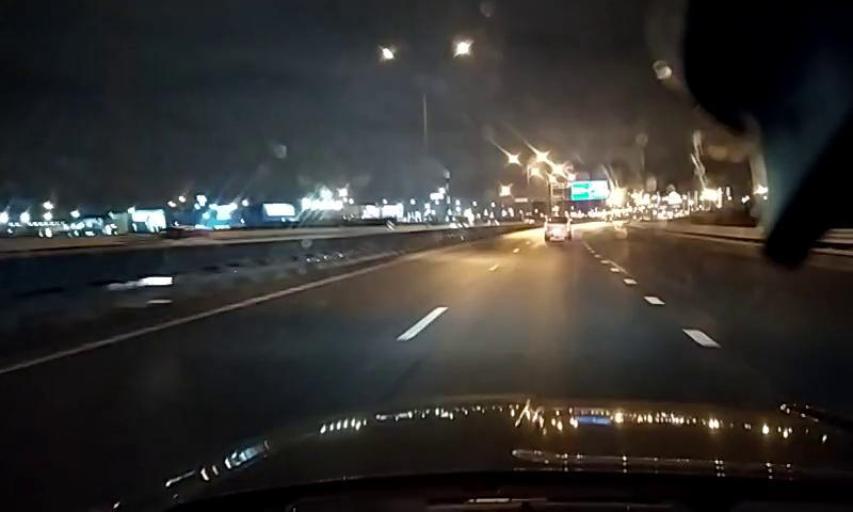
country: RU
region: Leningrad
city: Bugry
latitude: 60.0974
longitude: 30.3806
